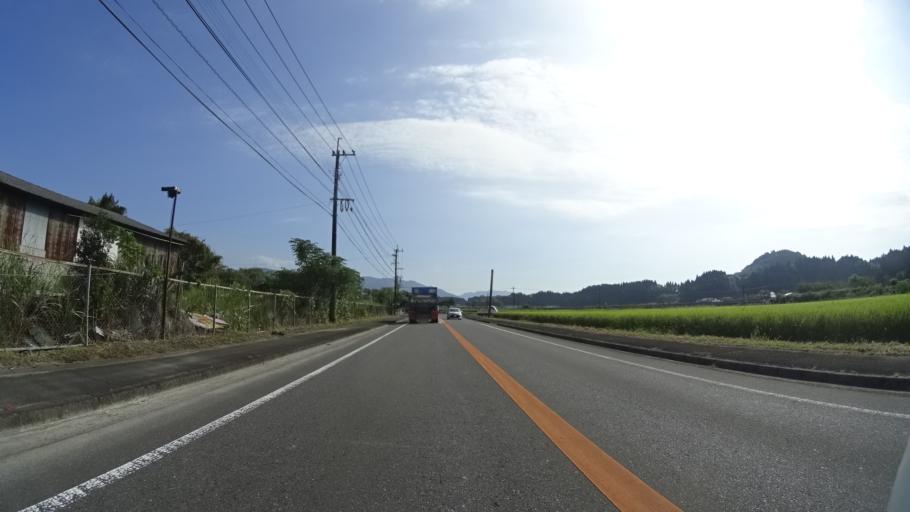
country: JP
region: Kagoshima
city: Okuchi-shinohara
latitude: 32.0409
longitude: 130.7605
